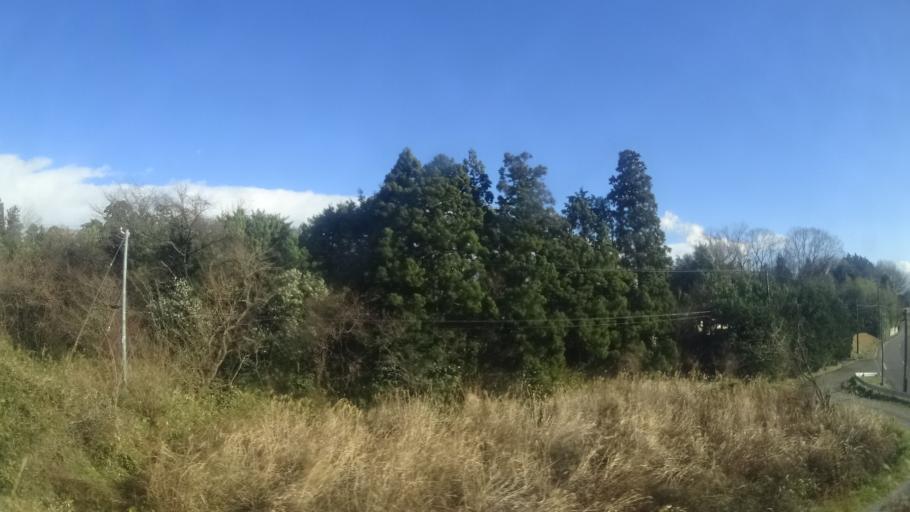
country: JP
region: Miyagi
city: Marumori
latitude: 37.8544
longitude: 140.9298
